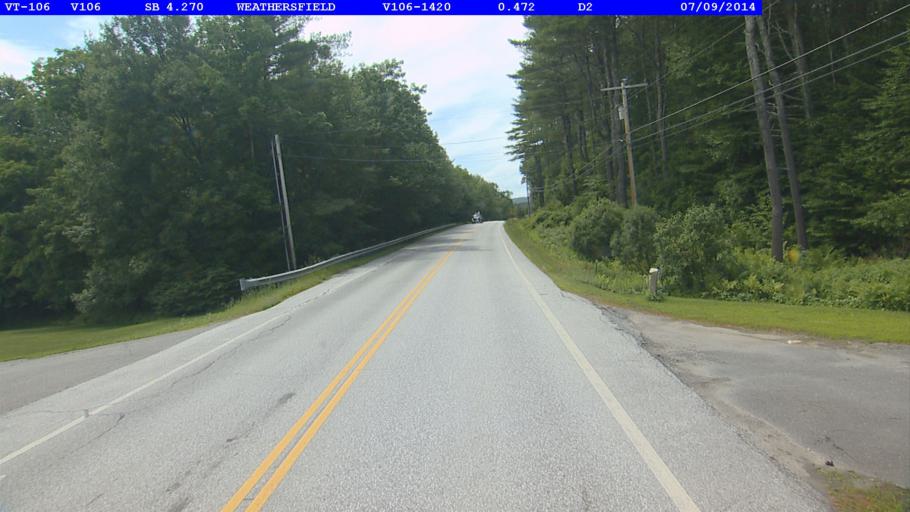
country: US
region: Vermont
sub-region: Windsor County
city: Springfield
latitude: 43.3501
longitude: -72.5258
